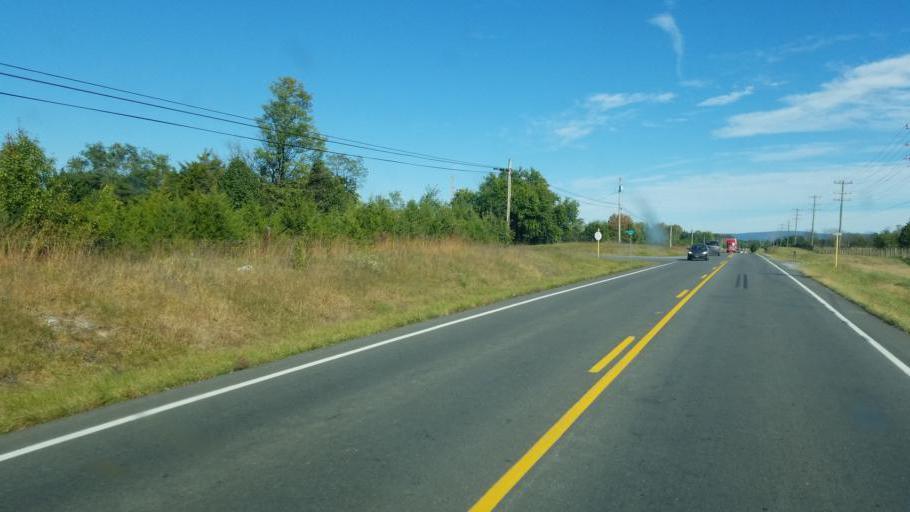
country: US
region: Virginia
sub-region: Warren County
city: Shenandoah Farms
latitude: 39.0592
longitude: -78.1270
